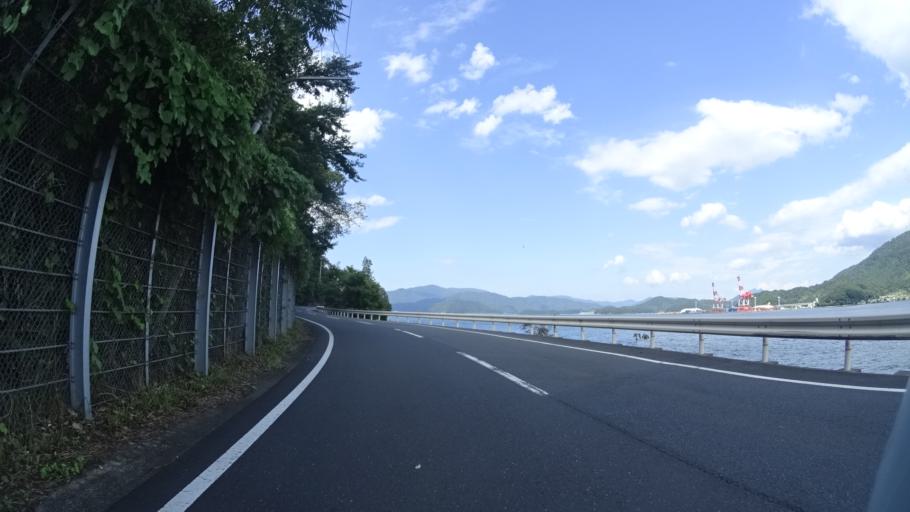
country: JP
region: Kyoto
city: Maizuru
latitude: 35.4675
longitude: 135.3187
